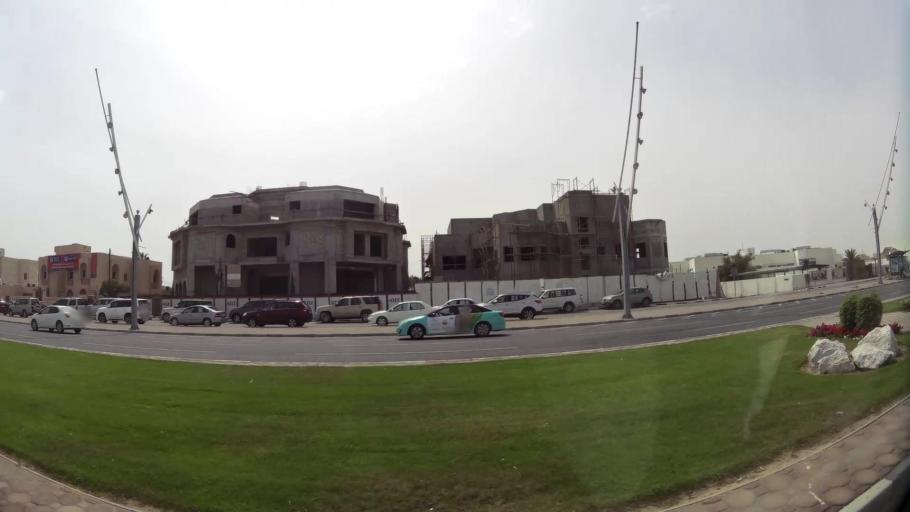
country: QA
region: Baladiyat ad Dawhah
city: Doha
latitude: 25.2709
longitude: 51.4791
